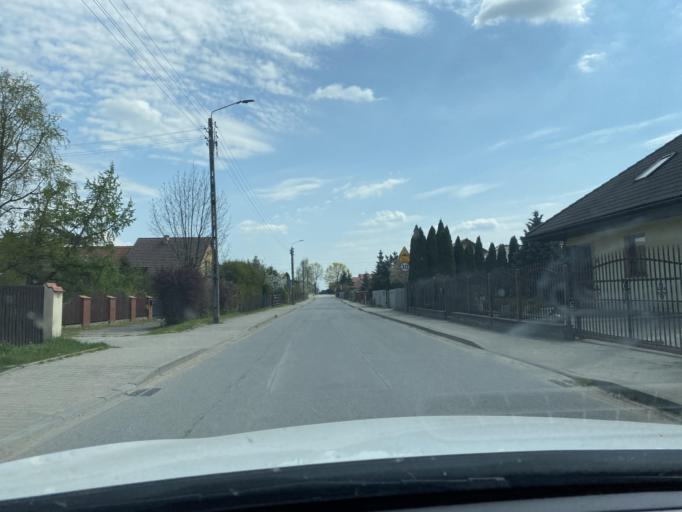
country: PL
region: Lower Silesian Voivodeship
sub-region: Powiat wroclawski
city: Mirkow
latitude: 51.1608
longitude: 17.1695
